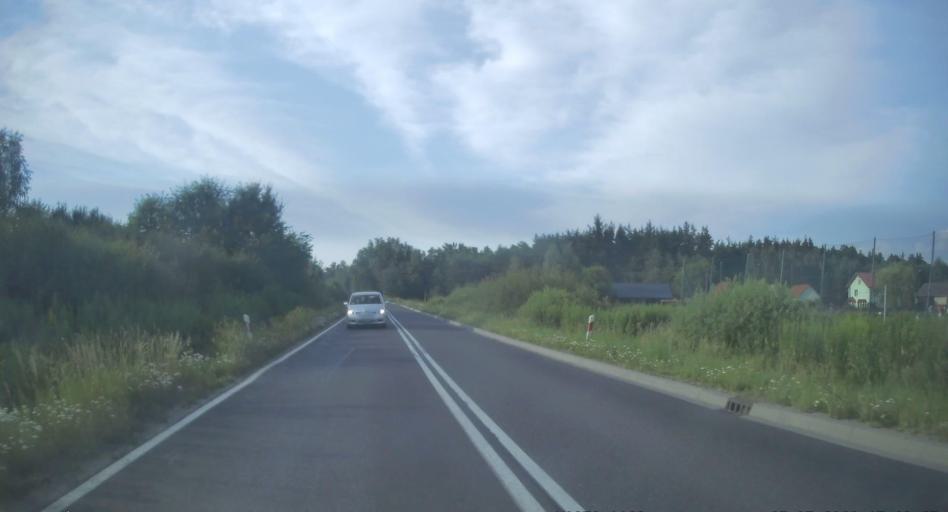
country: PL
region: Lesser Poland Voivodeship
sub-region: Powiat brzeski
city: Przyborow
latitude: 50.0408
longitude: 20.6460
